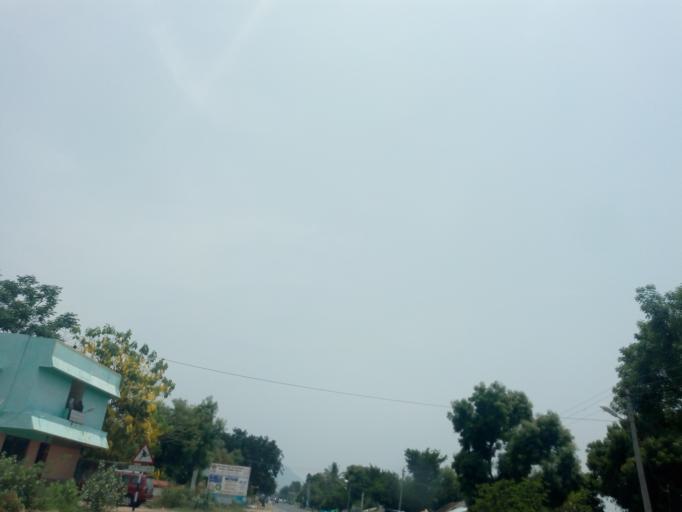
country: IN
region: Tamil Nadu
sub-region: Vellore
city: Vellore
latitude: 12.8710
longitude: 79.0950
